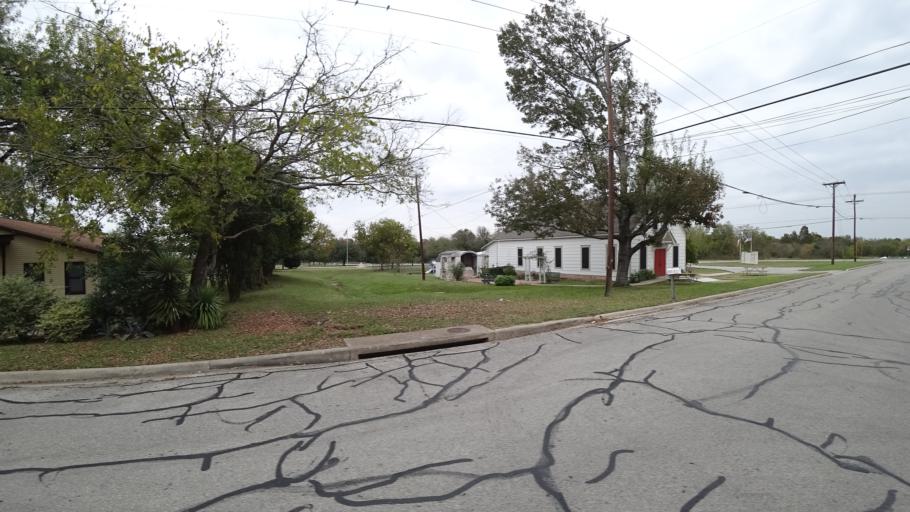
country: US
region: Texas
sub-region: Travis County
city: Pflugerville
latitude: 30.4424
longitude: -97.6195
